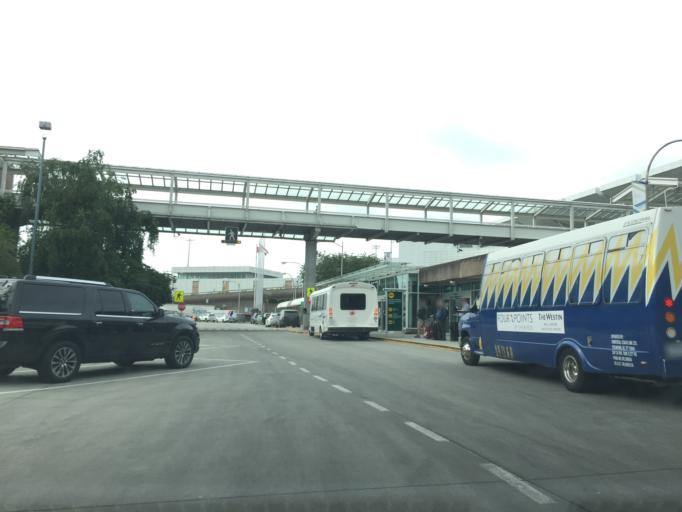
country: CA
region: British Columbia
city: Richmond
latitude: 49.1939
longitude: -123.1796
